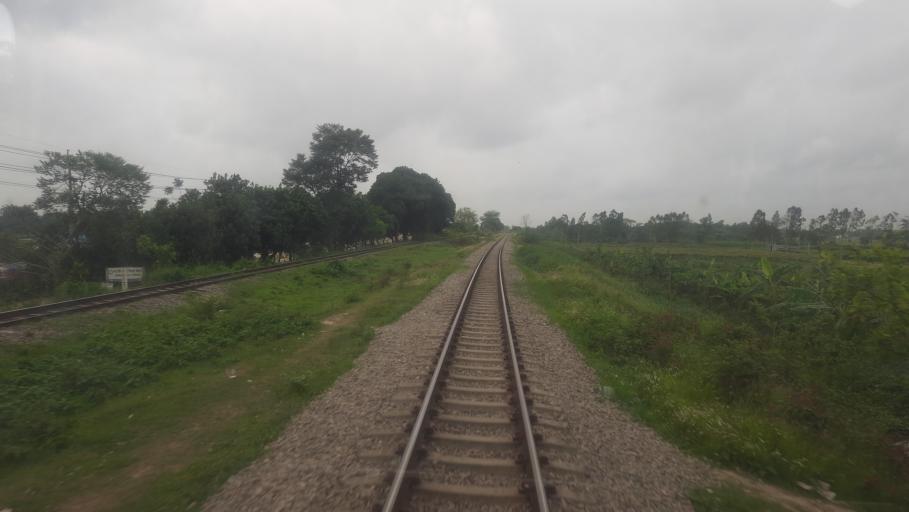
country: BD
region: Dhaka
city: Narsingdi
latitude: 23.9325
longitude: 90.7573
